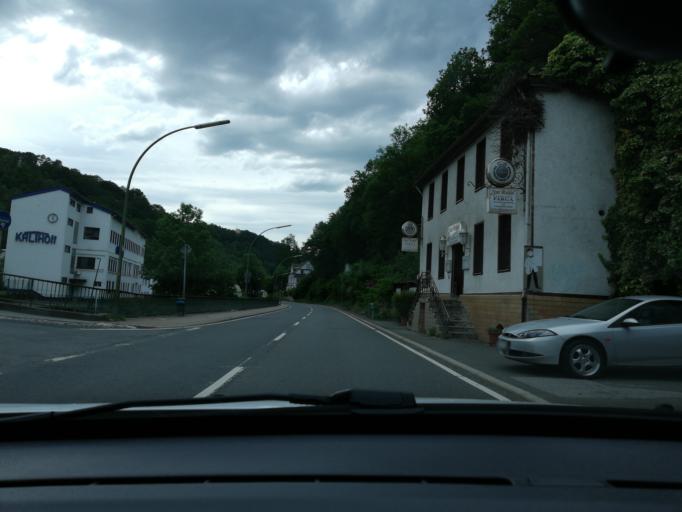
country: DE
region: North Rhine-Westphalia
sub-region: Regierungsbezirk Arnsberg
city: Schalksmuhle
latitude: 51.2436
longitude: 7.5292
